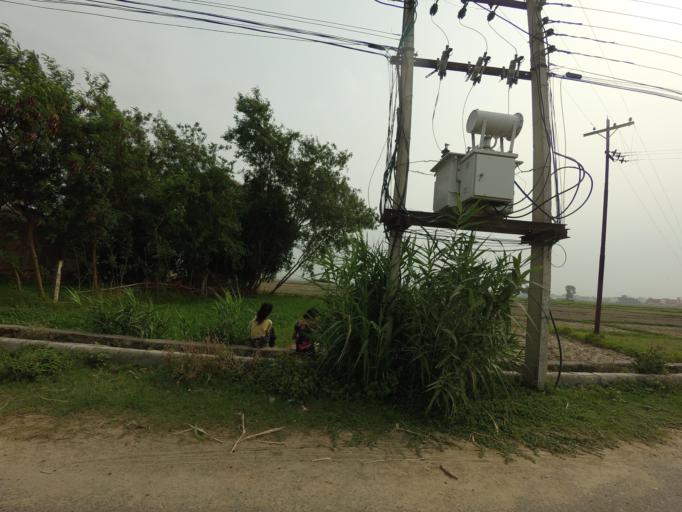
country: NP
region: Western Region
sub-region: Lumbini Zone
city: Bhairahawa
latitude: 27.4889
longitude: 83.4348
